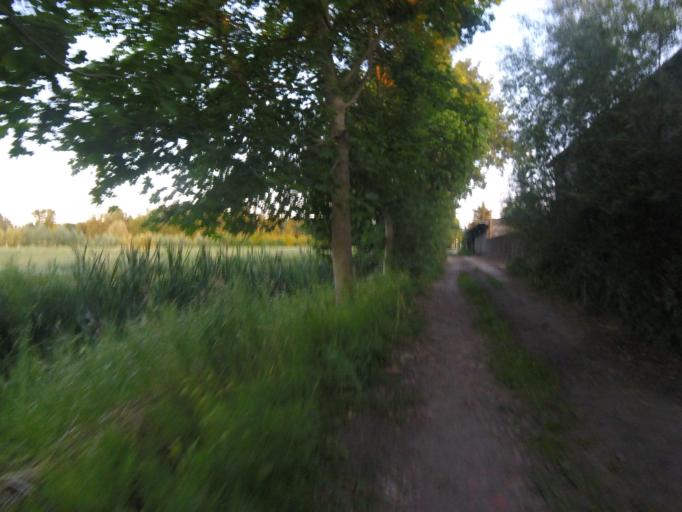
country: DE
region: Brandenburg
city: Konigs Wusterhausen
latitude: 52.2839
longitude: 13.5926
